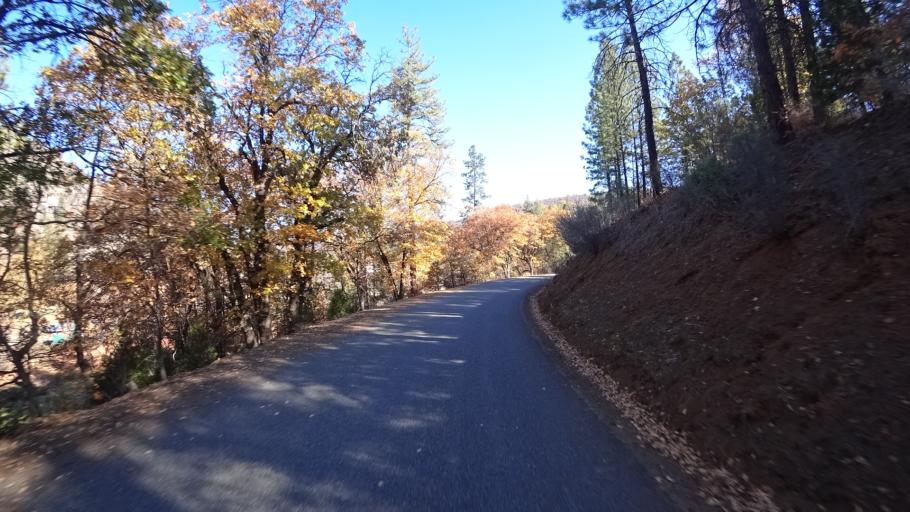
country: US
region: California
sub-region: Siskiyou County
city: Yreka
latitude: 41.8342
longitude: -122.8411
